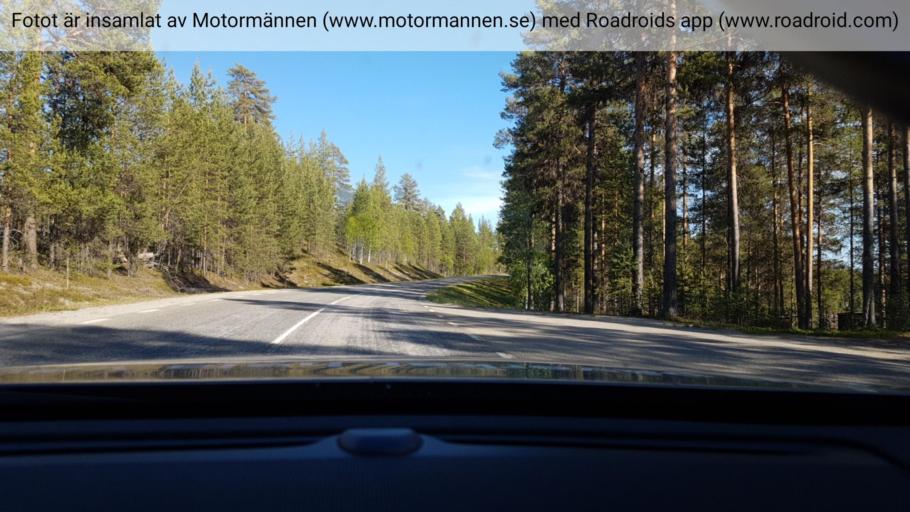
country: SE
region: Vaesterbotten
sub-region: Norsjo Kommun
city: Norsjoe
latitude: 64.7507
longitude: 19.0935
